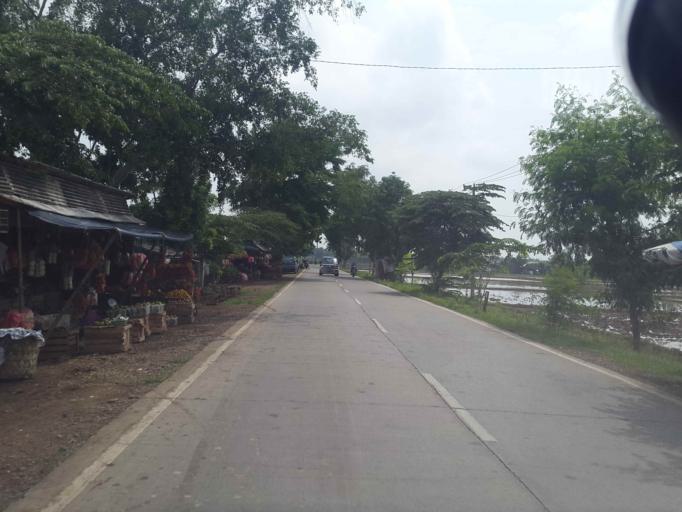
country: ID
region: West Java
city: Rengasdengklok
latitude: -6.2919
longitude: 107.3557
